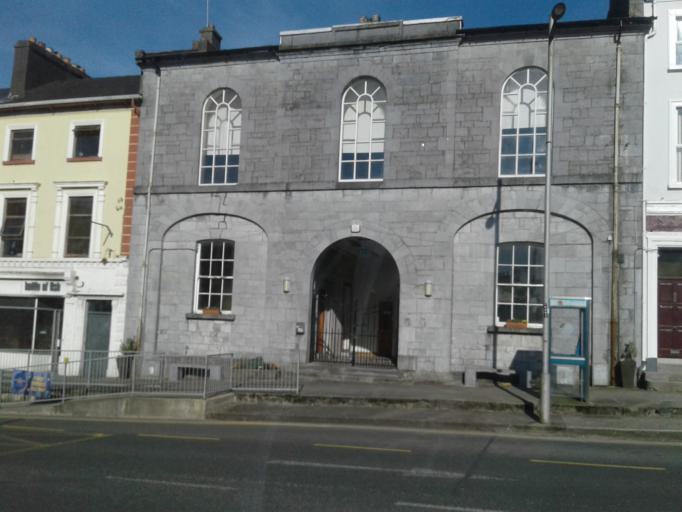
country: IE
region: Connaught
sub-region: County Galway
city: Gort
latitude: 53.0672
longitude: -8.8192
